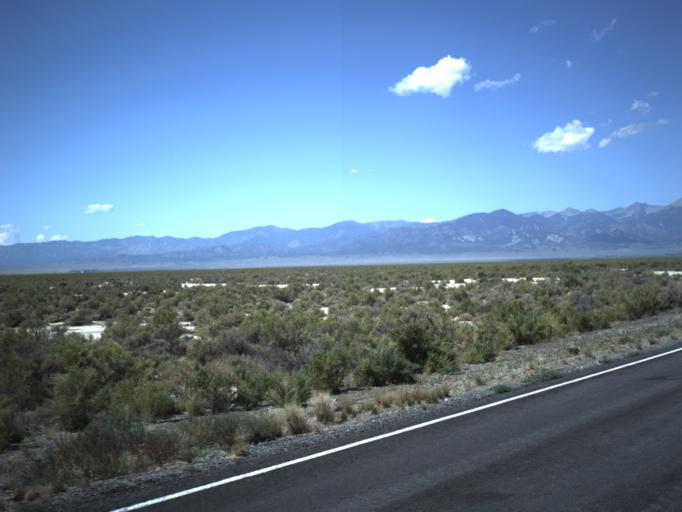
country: US
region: Nevada
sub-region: White Pine County
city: McGill
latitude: 39.0460
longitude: -113.9030
